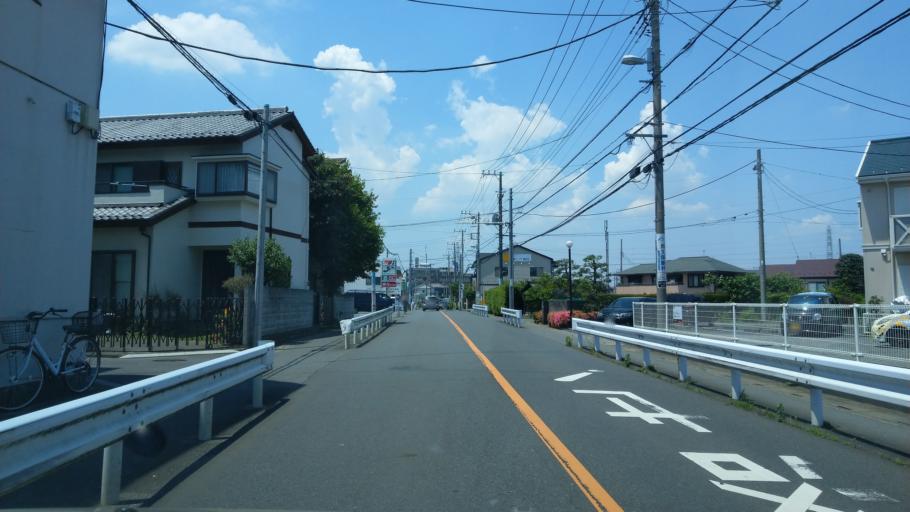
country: JP
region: Saitama
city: Shimotoda
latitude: 35.8609
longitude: 139.6869
